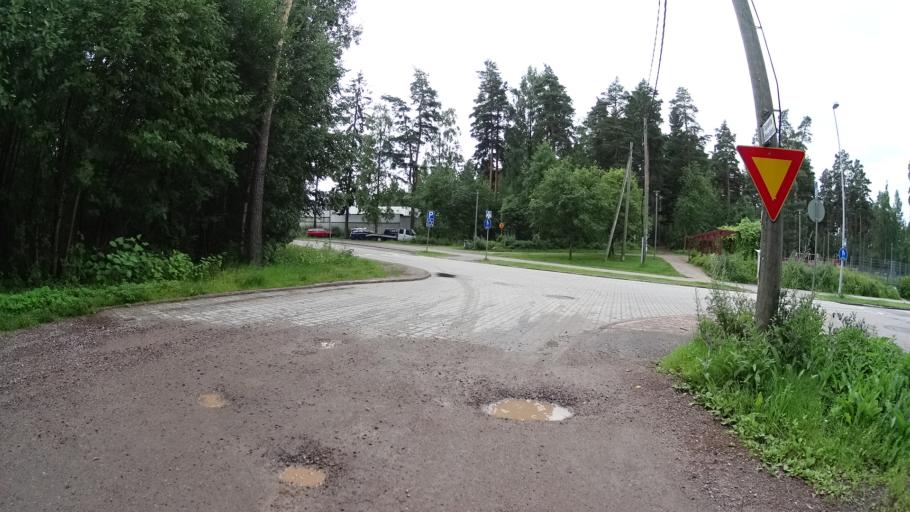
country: FI
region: Uusimaa
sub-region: Helsinki
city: Kilo
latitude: 60.2310
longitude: 24.8065
